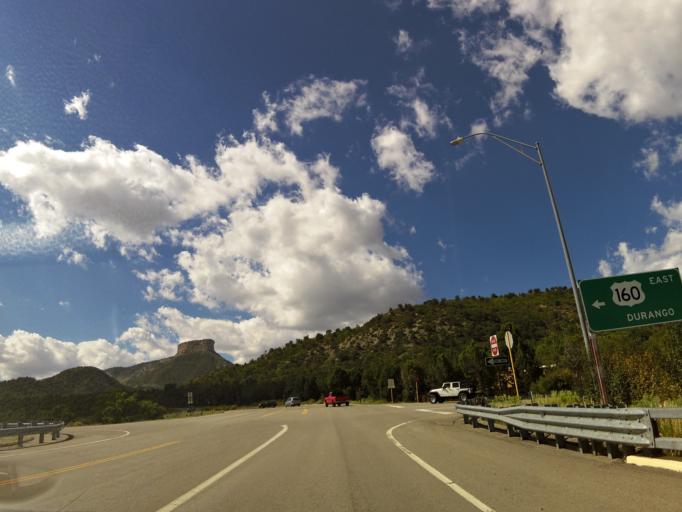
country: US
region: Colorado
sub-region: Montezuma County
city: Mancos
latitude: 37.3406
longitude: -108.4116
